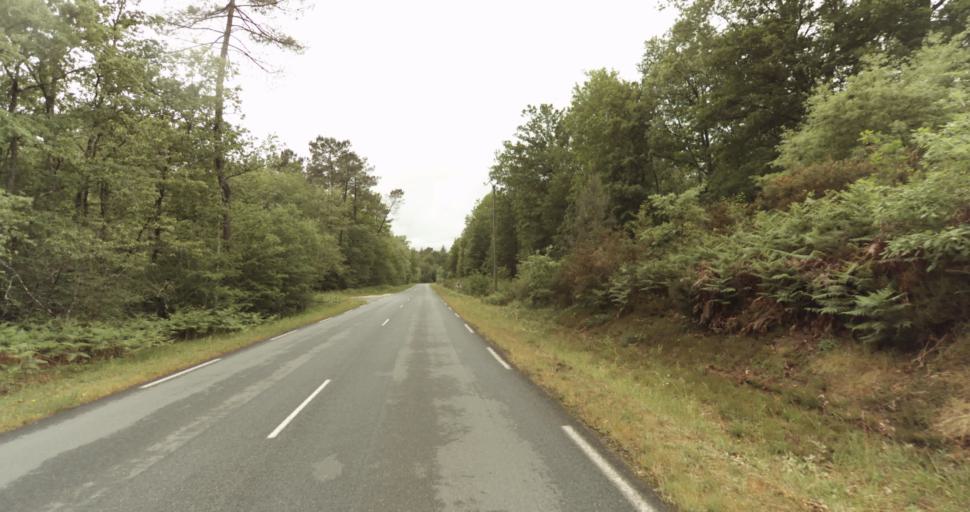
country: FR
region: Aquitaine
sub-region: Departement de la Dordogne
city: Belves
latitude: 44.6879
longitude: 0.9820
